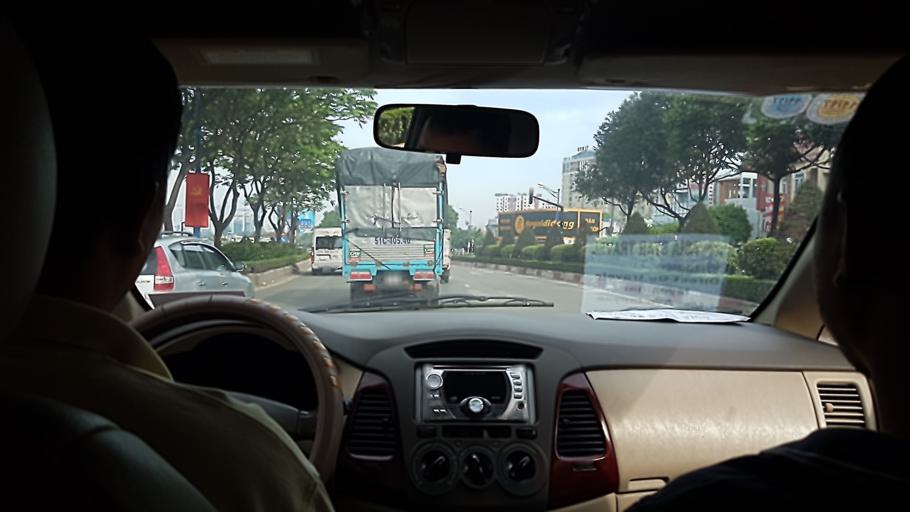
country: VN
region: Ho Chi Minh City
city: Ho Chi Minh City
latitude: 10.8225
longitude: 106.6301
